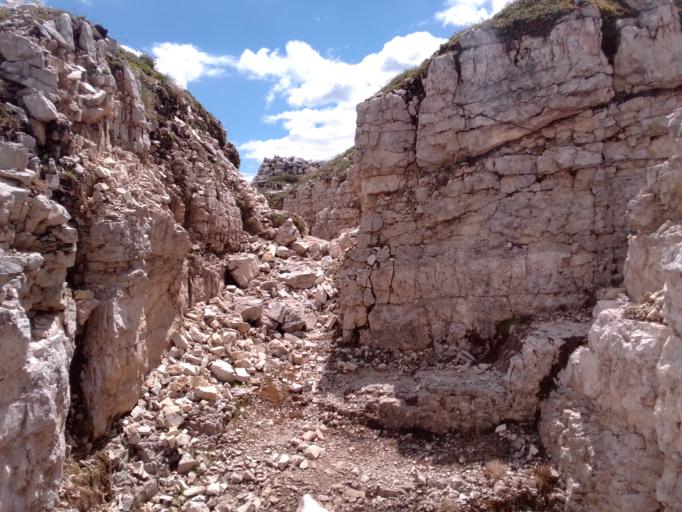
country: IT
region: Trentino-Alto Adige
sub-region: Bolzano
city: Dobbiaco
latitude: 46.6167
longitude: 12.2477
